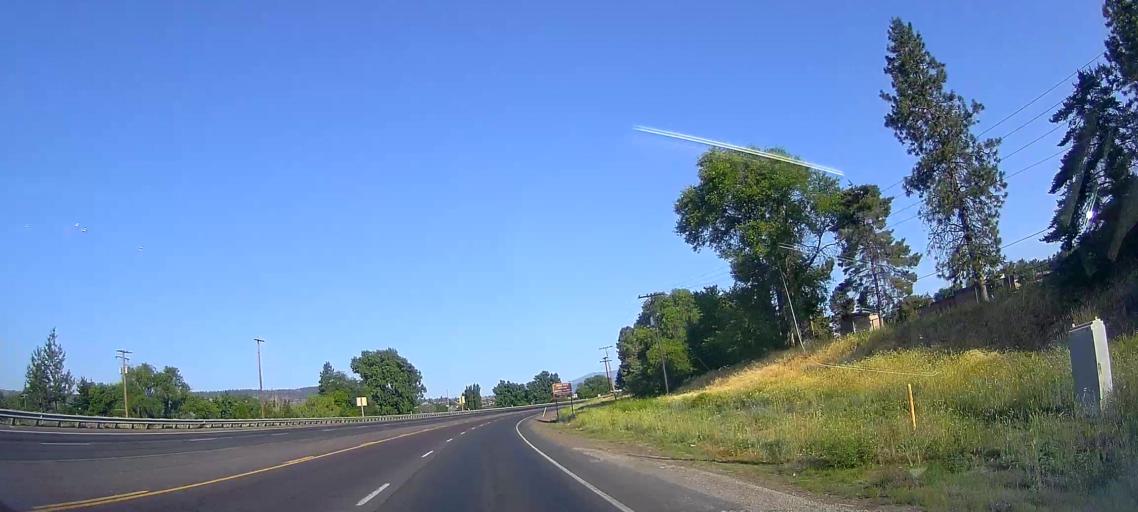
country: US
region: Oregon
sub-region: Klamath County
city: Klamath Falls
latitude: 42.2255
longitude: -121.7597
